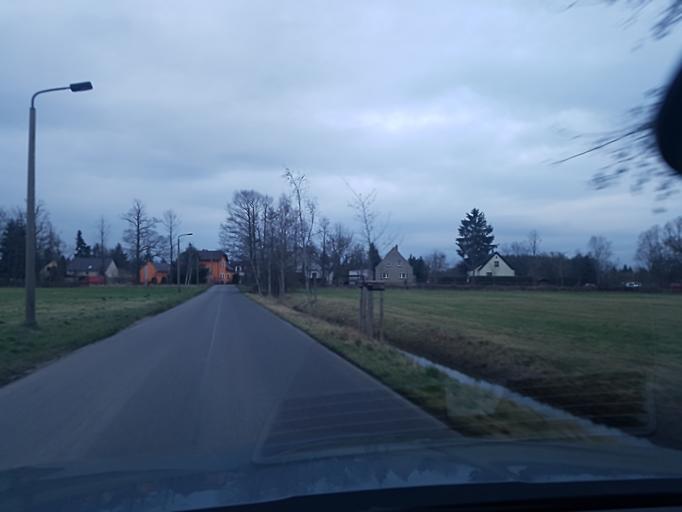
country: DE
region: Brandenburg
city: Doberlug-Kirchhain
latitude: 51.6111
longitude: 13.5569
